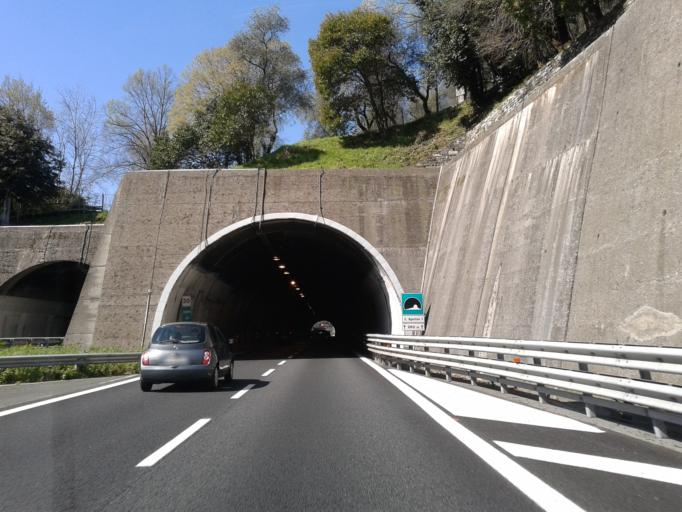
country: IT
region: Liguria
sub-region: Provincia di Genova
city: Rapallo
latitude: 44.3590
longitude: 9.2283
